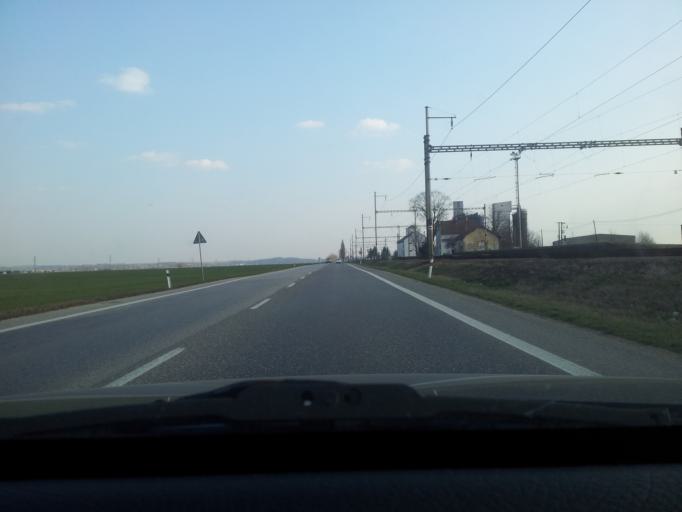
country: SK
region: Nitriansky
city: Tlmace
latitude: 48.2820
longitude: 18.5479
